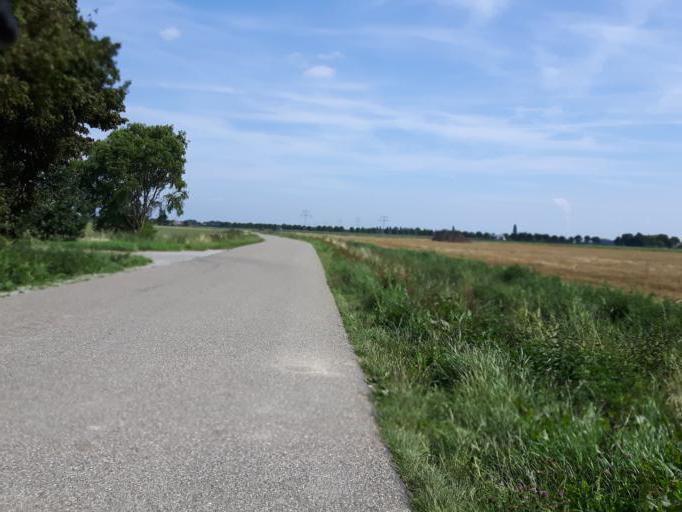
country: NL
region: Zeeland
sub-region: Gemeente Goes
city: Goes
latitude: 51.4777
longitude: 3.8763
